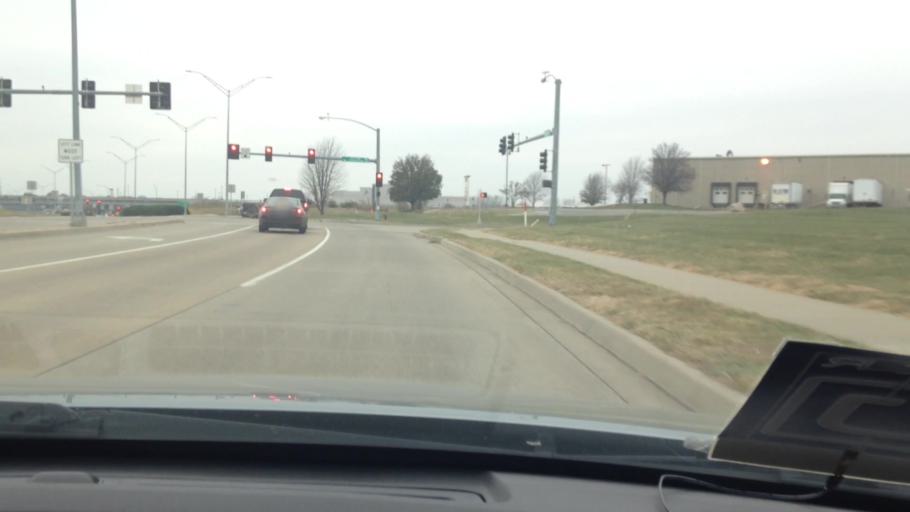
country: US
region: Missouri
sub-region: Cass County
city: Belton
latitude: 38.8278
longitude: -94.5174
